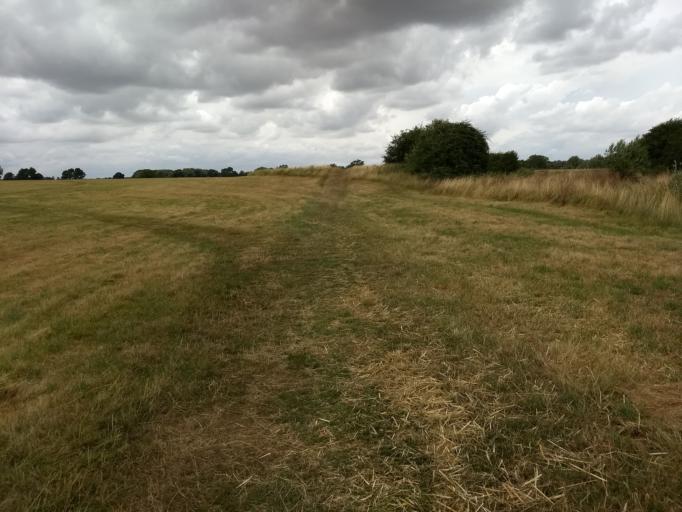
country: GB
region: England
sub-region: Milton Keynes
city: Newport Pagnell
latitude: 52.0896
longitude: -0.7289
